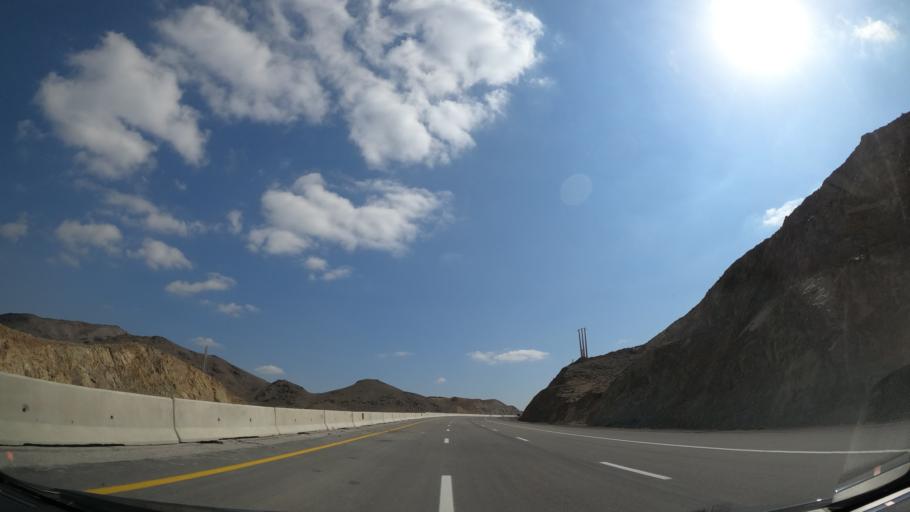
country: IR
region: Alborz
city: Nazarabad
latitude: 35.6838
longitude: 50.6401
